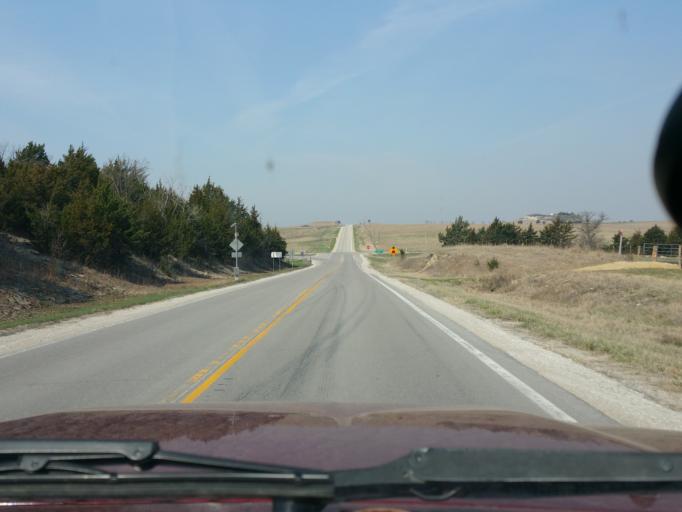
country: US
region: Kansas
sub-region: Marshall County
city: Blue Rapids
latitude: 39.4362
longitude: -96.7610
